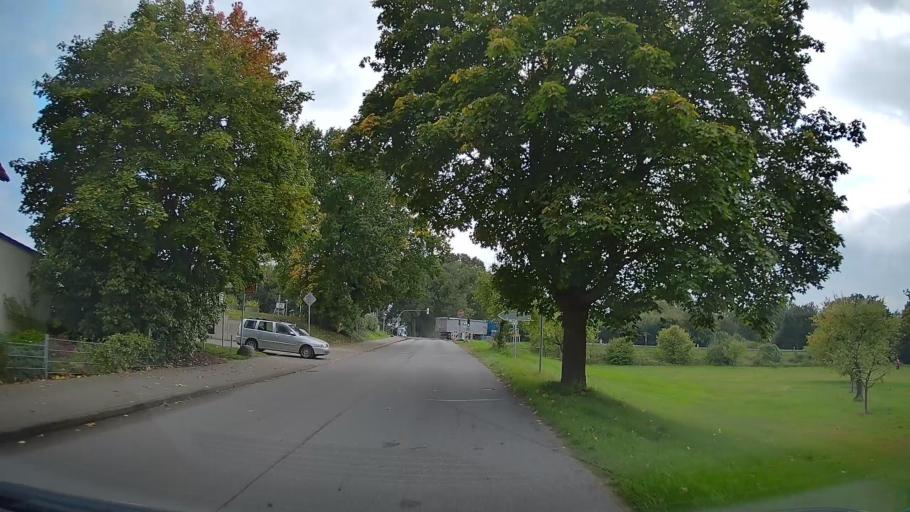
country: DE
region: Mecklenburg-Vorpommern
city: Lubtheen
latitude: 53.3951
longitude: 10.9648
